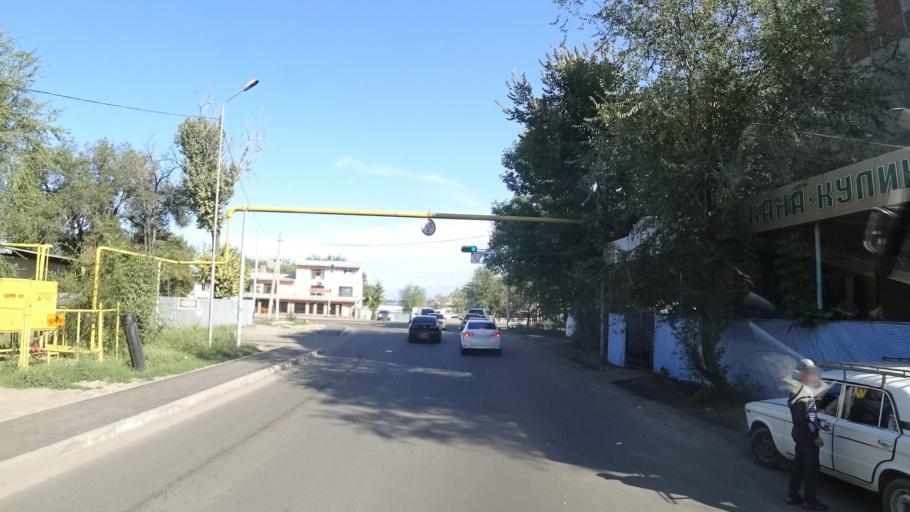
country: KZ
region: Almaty Oblysy
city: Energeticheskiy
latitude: 43.4256
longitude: 77.0238
